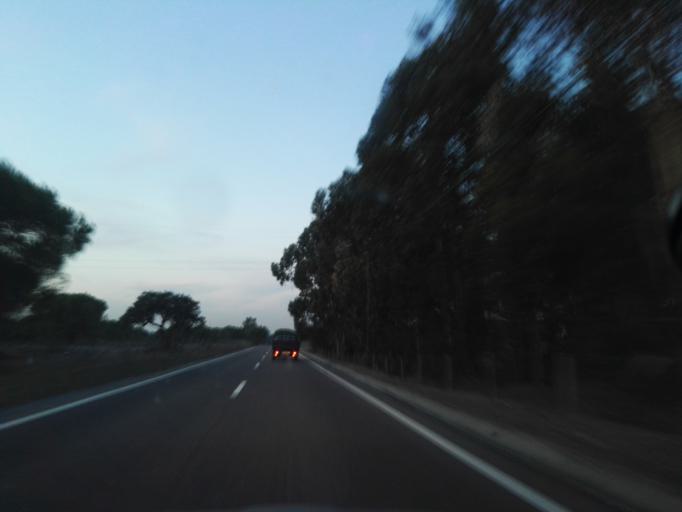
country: PT
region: Santarem
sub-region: Benavente
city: Benavente
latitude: 38.9269
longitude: -8.7768
